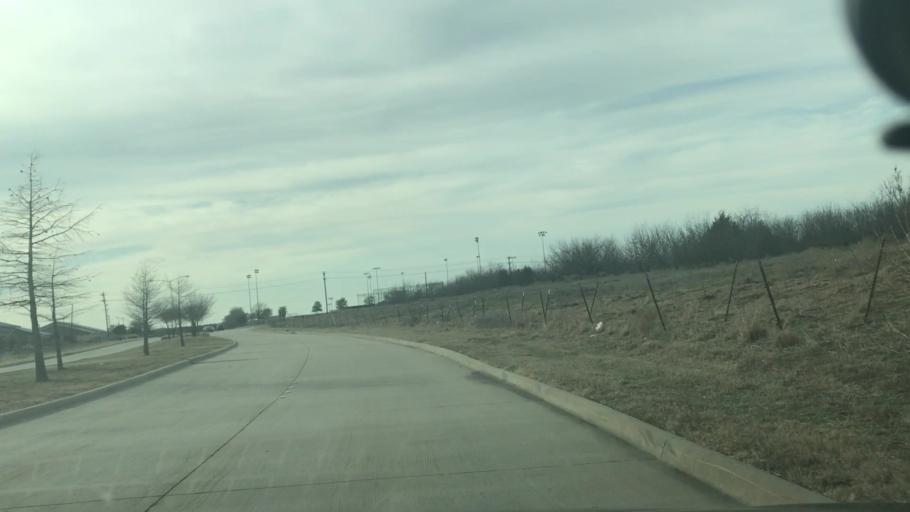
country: US
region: Texas
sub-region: Dallas County
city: Coppell
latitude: 33.0001
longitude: -97.0254
